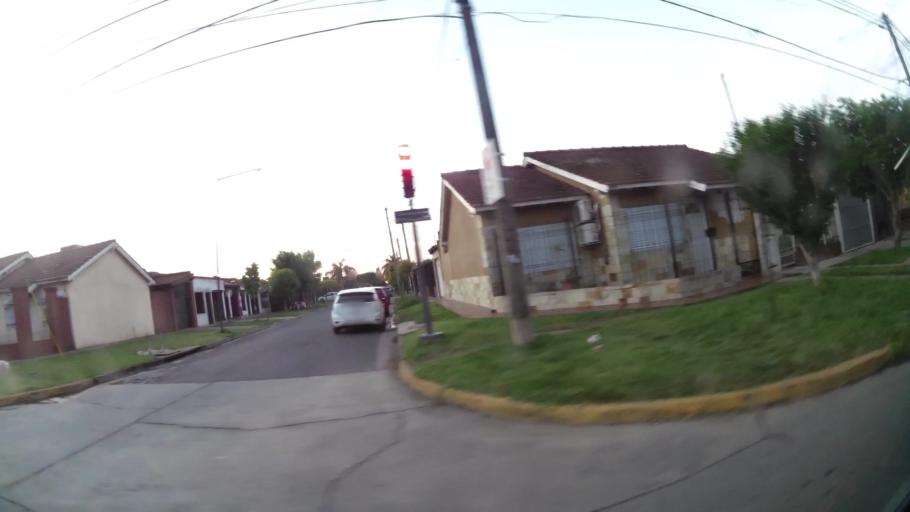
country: AR
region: Buenos Aires
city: San Nicolas de los Arroyos
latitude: -33.3505
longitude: -60.1970
